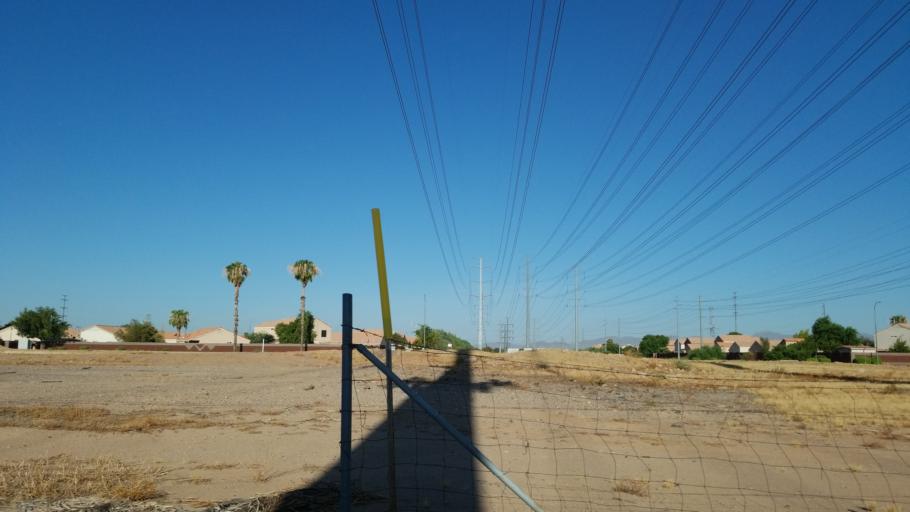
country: US
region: Arizona
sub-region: Maricopa County
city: Avondale
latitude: 33.4664
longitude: -112.3142
